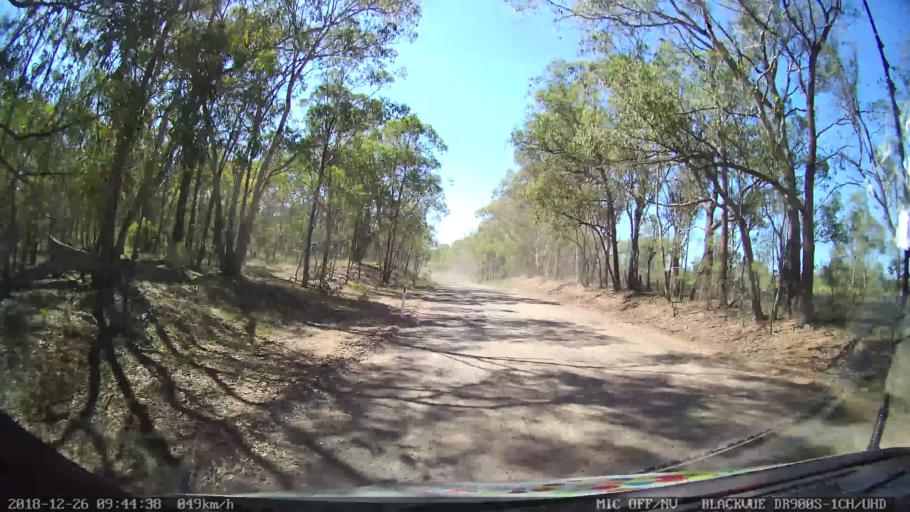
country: AU
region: New South Wales
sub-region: Mid-Western Regional
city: Kandos
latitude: -32.9581
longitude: 150.0978
